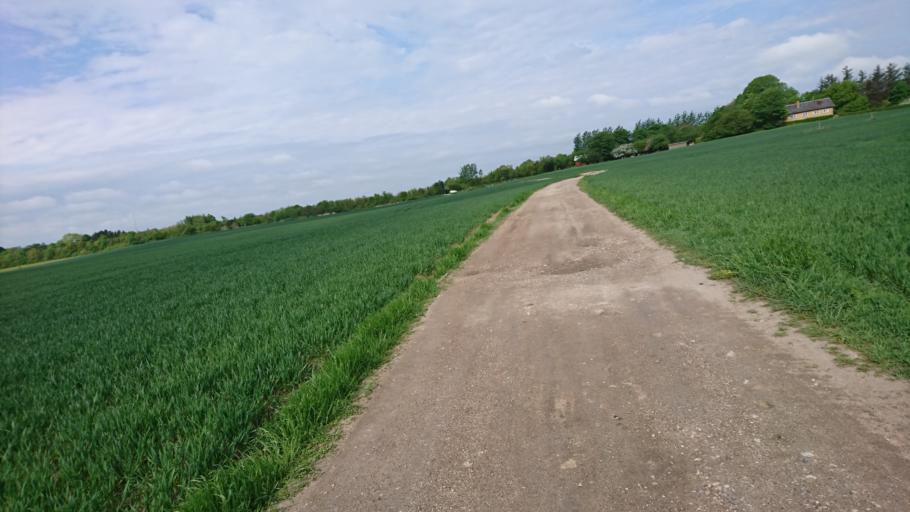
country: DK
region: Capital Region
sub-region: Egedal Kommune
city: Smorumnedre
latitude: 55.7354
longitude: 12.3166
